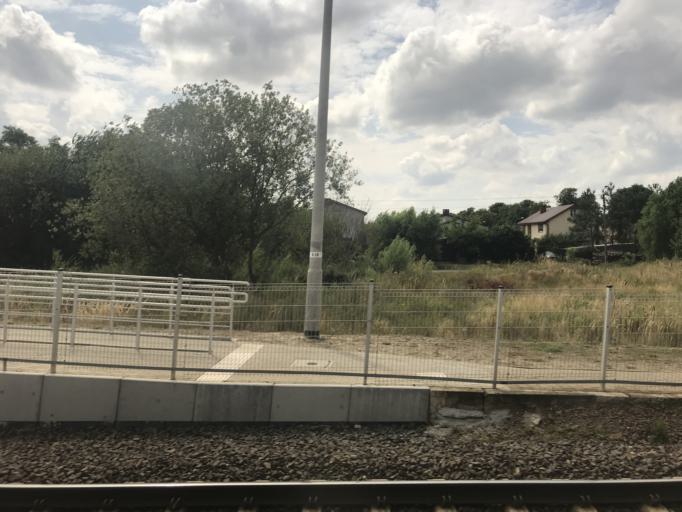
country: PL
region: Greater Poland Voivodeship
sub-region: Powiat gnieznienski
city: Lubowo
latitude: 52.4984
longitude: 17.4226
